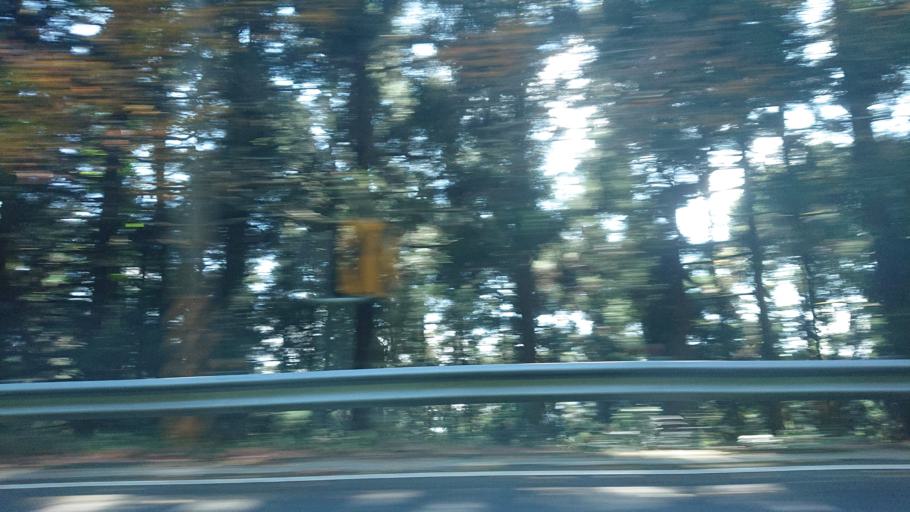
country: TW
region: Taiwan
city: Lugu
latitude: 23.5030
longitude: 120.8110
